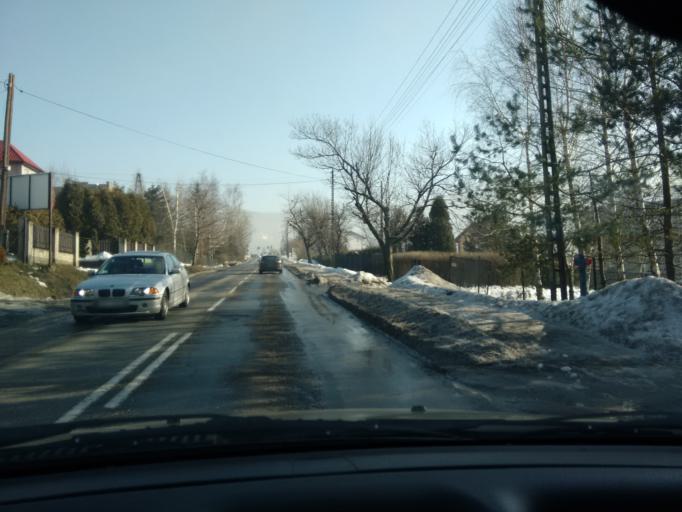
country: PL
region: Silesian Voivodeship
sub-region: Powiat bielski
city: Kozy
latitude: 49.8253
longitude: 19.1076
